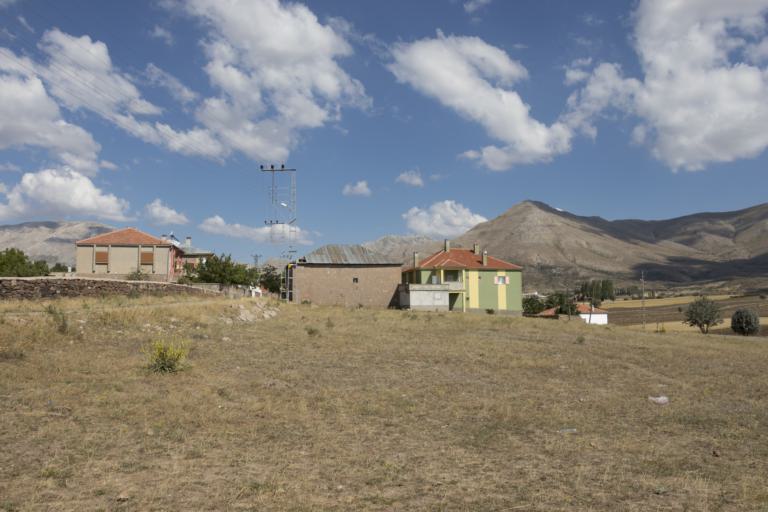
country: TR
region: Kayseri
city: Toklar
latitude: 38.4072
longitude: 36.0770
